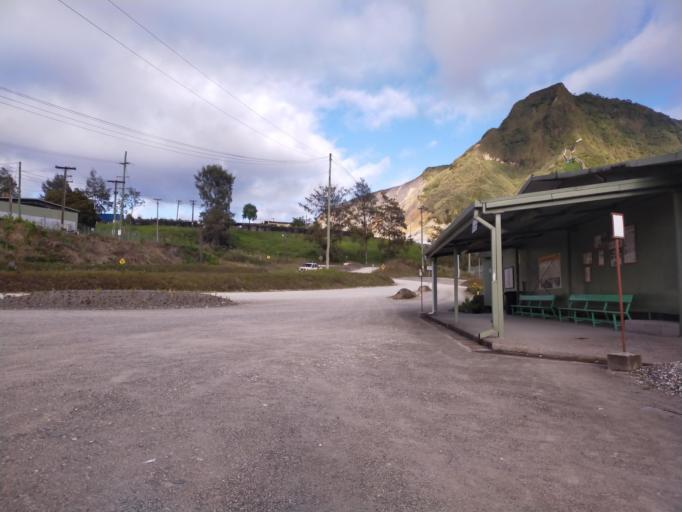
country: PG
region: Enga
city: Porgera
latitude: -5.4633
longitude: 143.1038
